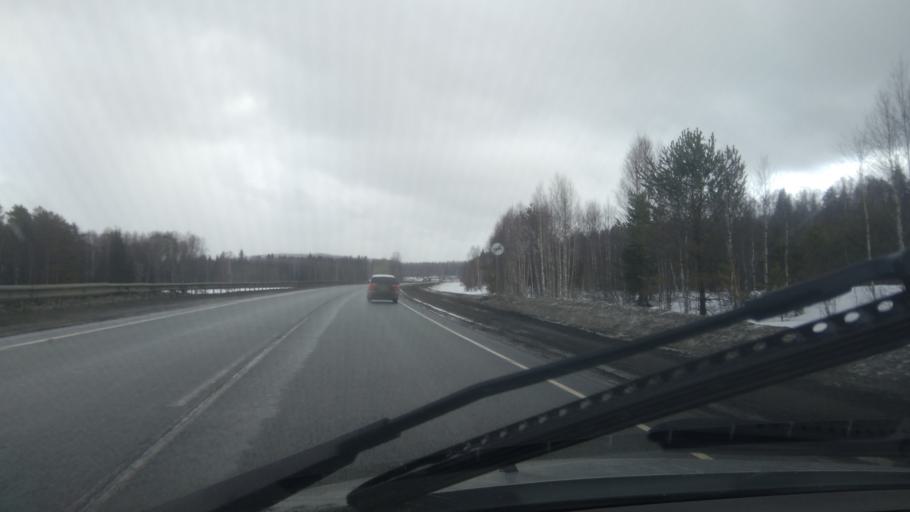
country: RU
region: Sverdlovsk
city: Ufimskiy
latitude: 56.7856
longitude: 58.3902
